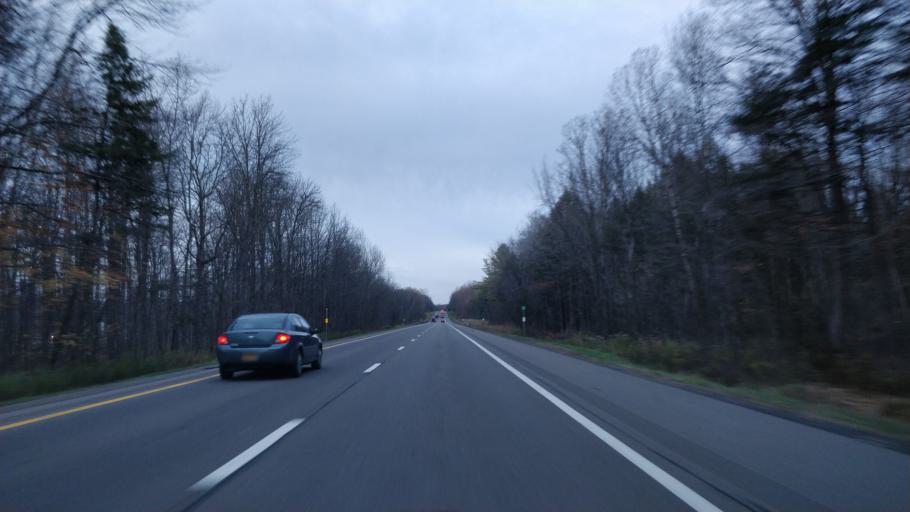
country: US
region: New York
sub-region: Oswego County
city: Central Square
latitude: 43.3497
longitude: -76.1219
